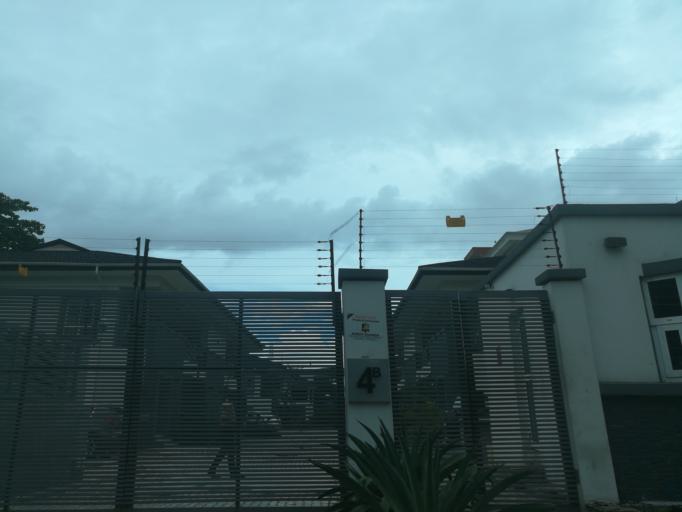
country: NG
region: Lagos
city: Ikoyi
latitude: 6.4343
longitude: 3.4214
